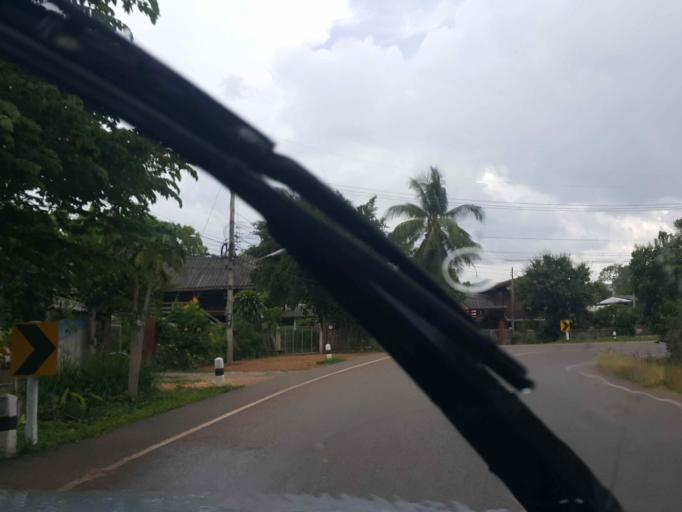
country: TH
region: Phayao
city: Dok Kham Tai
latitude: 19.0512
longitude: 100.0522
